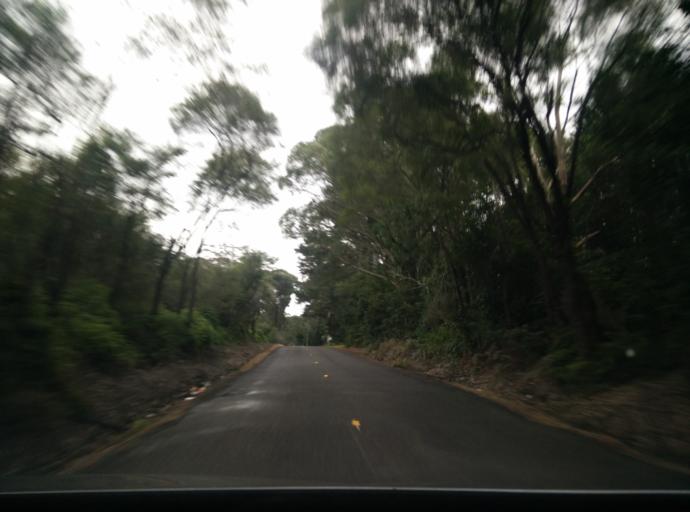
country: AU
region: New South Wales
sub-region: Gosford Shire
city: Narara
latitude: -33.3527
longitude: 151.2967
